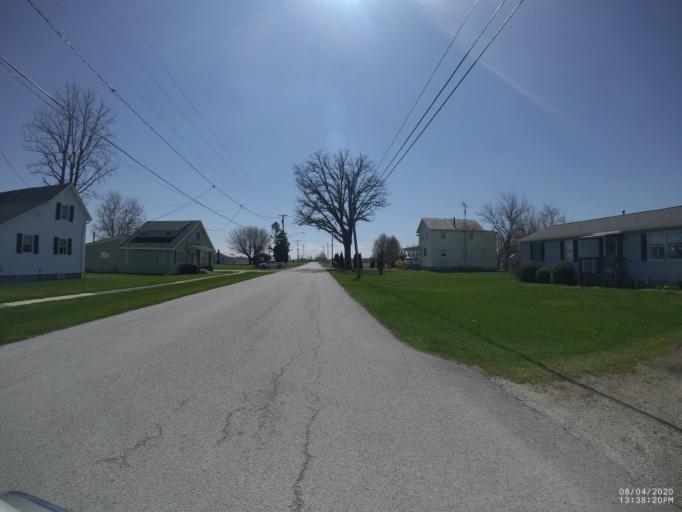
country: US
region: Ohio
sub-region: Sandusky County
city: Gibsonburg
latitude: 41.3379
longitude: -83.2918
